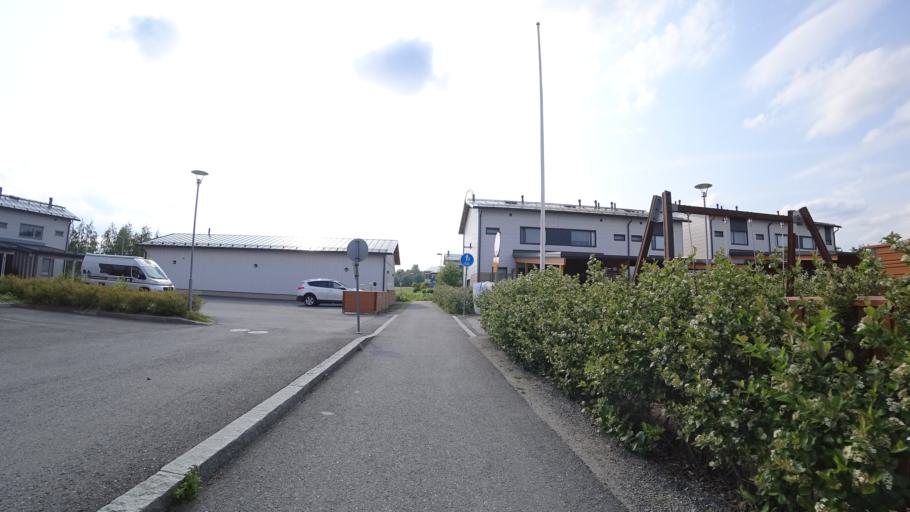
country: FI
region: Pirkanmaa
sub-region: Tampere
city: Pirkkala
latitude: 61.5037
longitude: 23.6870
